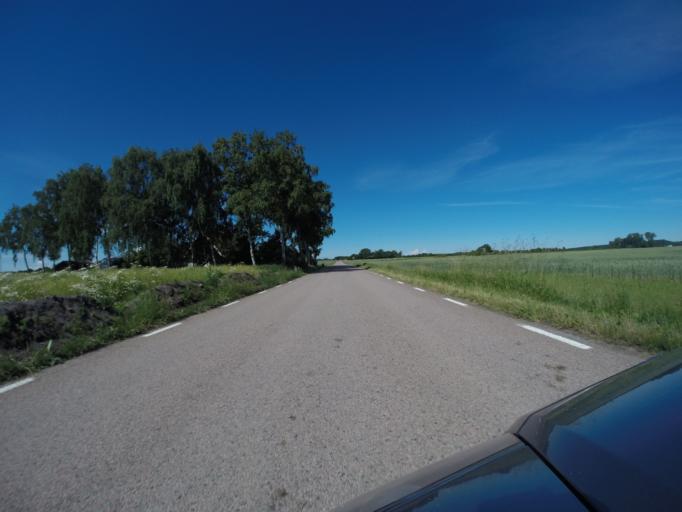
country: SE
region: Skane
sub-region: Helsingborg
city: Odakra
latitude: 56.1377
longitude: 12.7429
